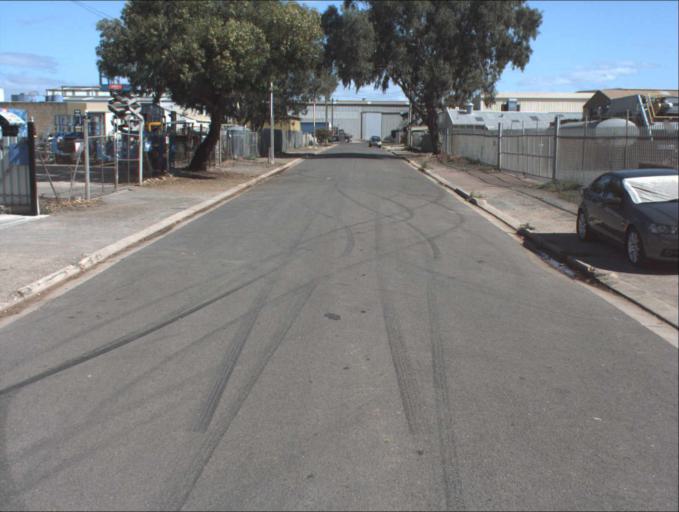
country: AU
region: South Australia
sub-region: Charles Sturt
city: Woodville North
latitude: -34.8353
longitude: 138.5577
